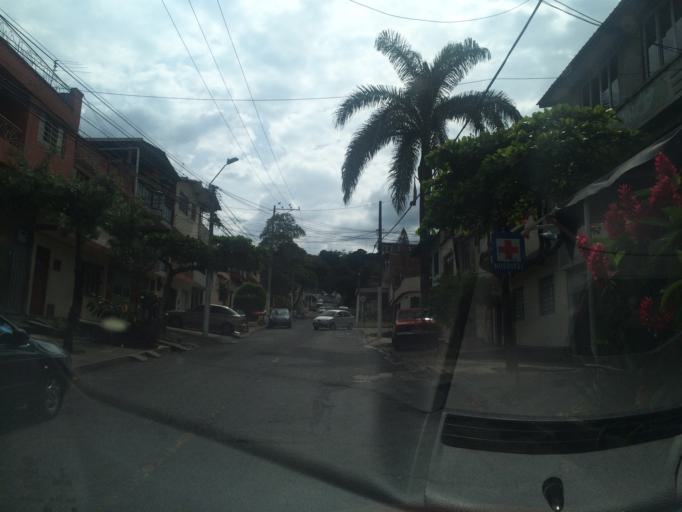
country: CO
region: Valle del Cauca
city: Cali
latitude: 3.4446
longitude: -76.5413
